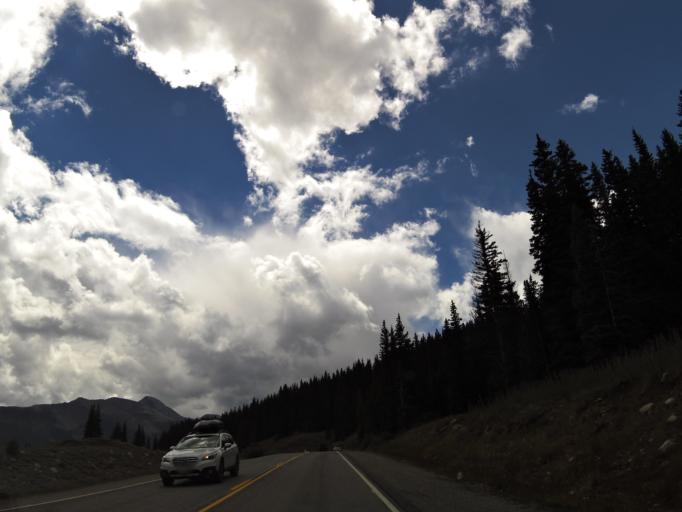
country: US
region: Colorado
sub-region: San Juan County
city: Silverton
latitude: 37.7634
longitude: -107.6798
